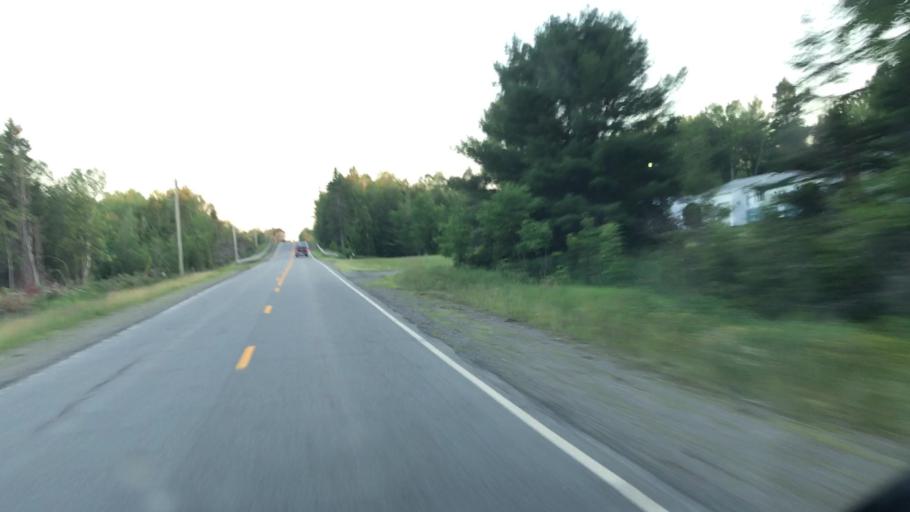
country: US
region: Maine
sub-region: Penobscot County
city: Medway
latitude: 45.6038
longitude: -68.3082
